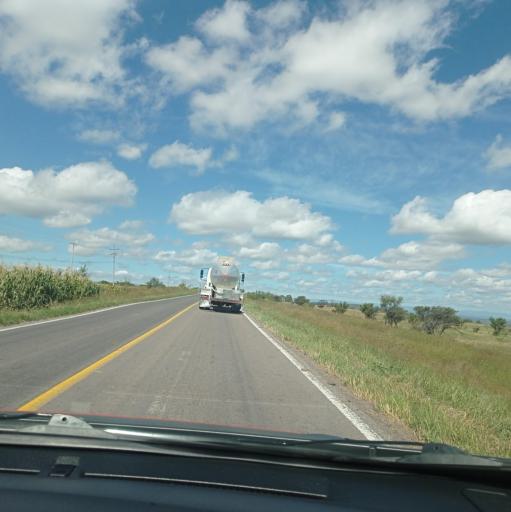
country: MX
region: Jalisco
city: Valle de Guadalupe
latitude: 21.0276
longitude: -102.5498
